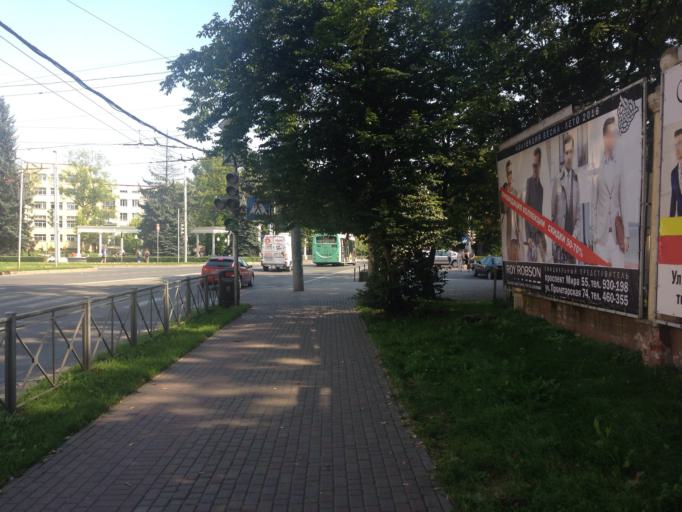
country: RU
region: Kaliningrad
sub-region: Gorod Kaliningrad
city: Kaliningrad
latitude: 54.7191
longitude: 20.4924
